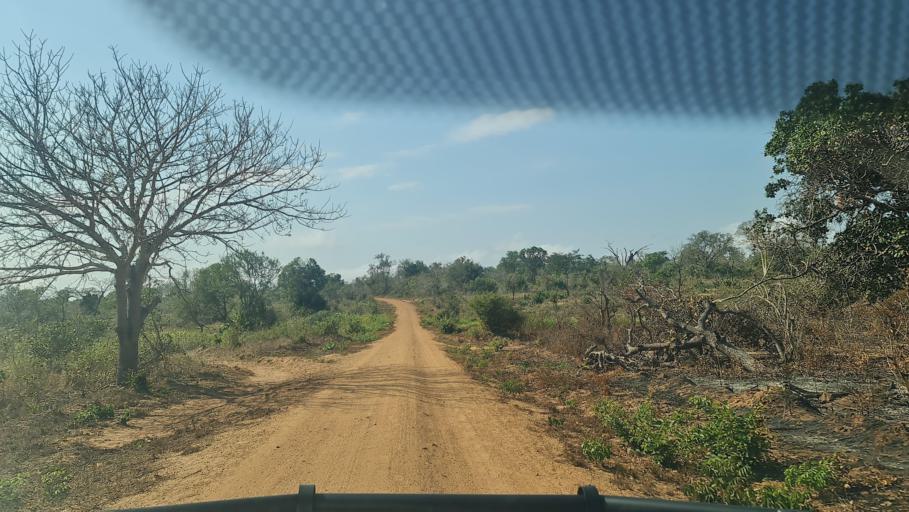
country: MZ
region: Nampula
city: Ilha de Mocambique
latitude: -15.1293
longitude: 40.2124
